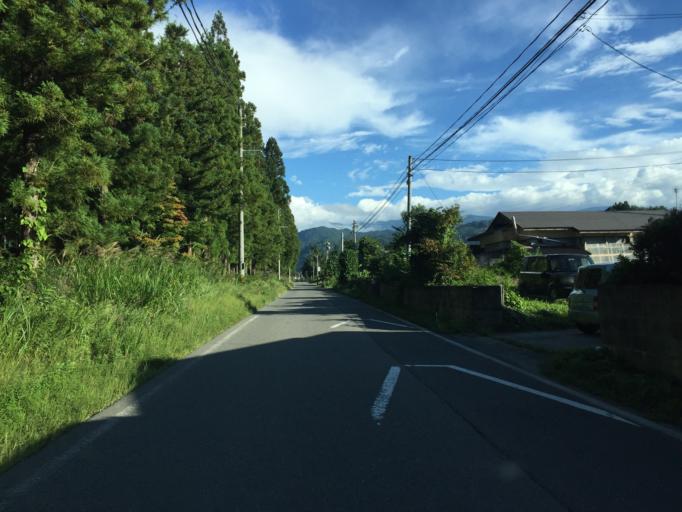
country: JP
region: Yamagata
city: Yonezawa
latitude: 37.8778
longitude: 140.1370
